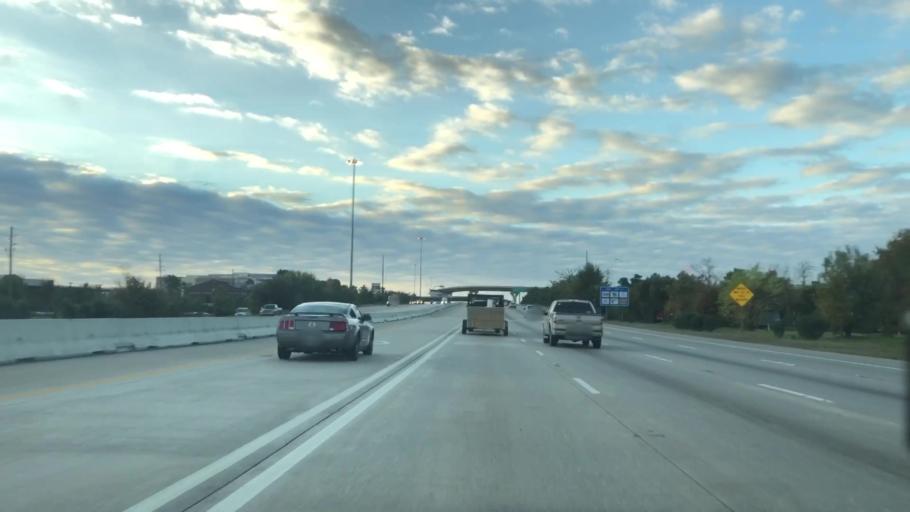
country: US
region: Texas
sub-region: Montgomery County
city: Shenandoah
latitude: 30.2125
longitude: -95.4568
